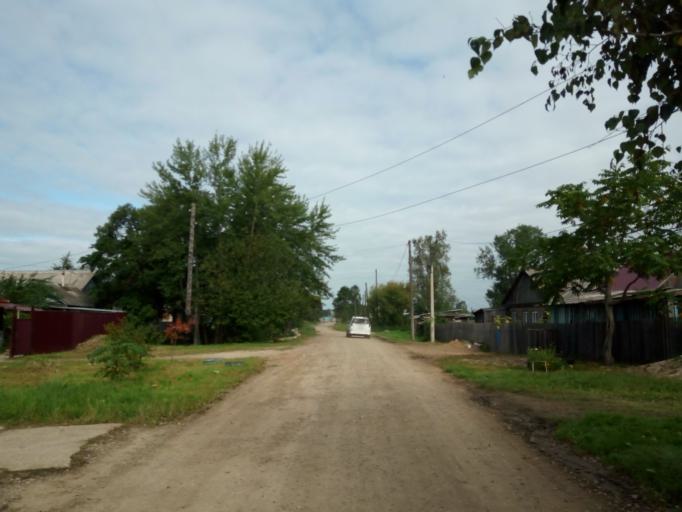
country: RU
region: Primorskiy
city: Dal'nerechensk
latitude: 45.9180
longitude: 133.7213
